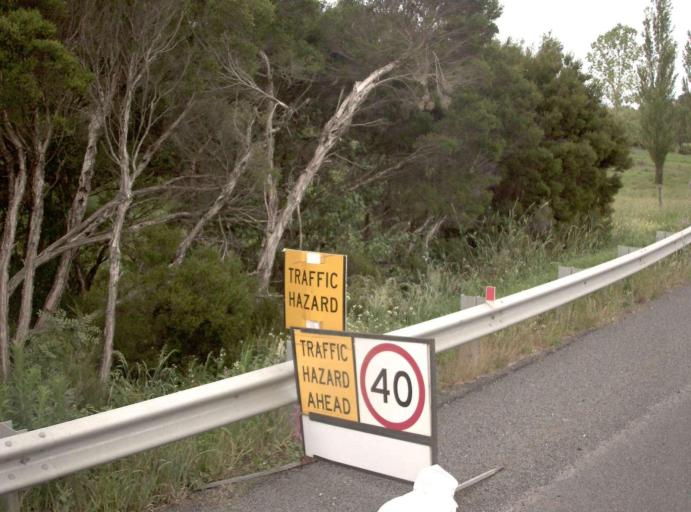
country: AU
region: Victoria
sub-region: Bass Coast
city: North Wonthaggi
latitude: -38.5263
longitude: 145.9518
